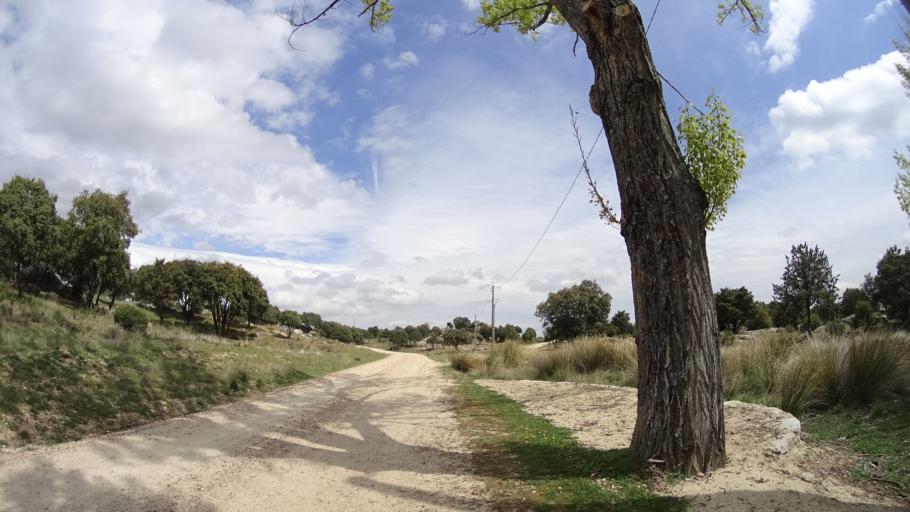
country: ES
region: Madrid
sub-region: Provincia de Madrid
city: Hoyo de Manzanares
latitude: 40.6225
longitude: -3.8821
